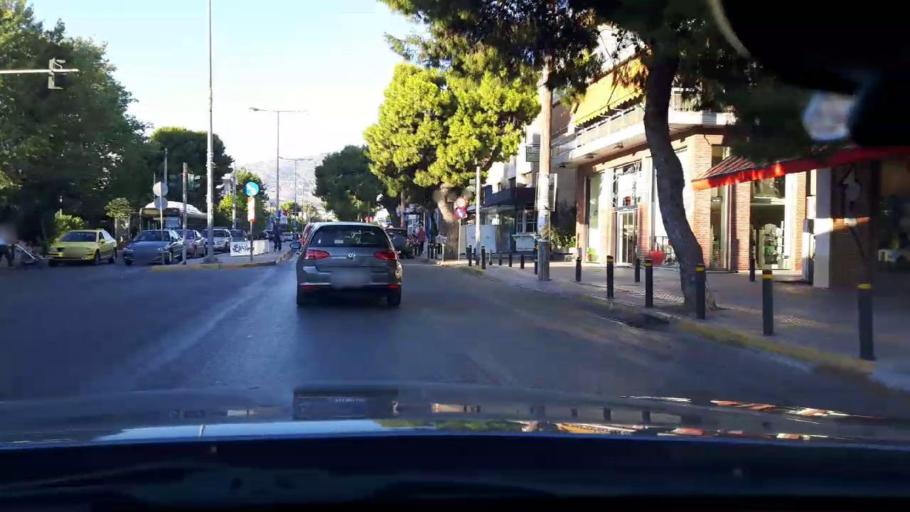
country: GR
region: Attica
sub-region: Nomarchia Athinas
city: Vrilissia
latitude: 38.0372
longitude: 23.8268
